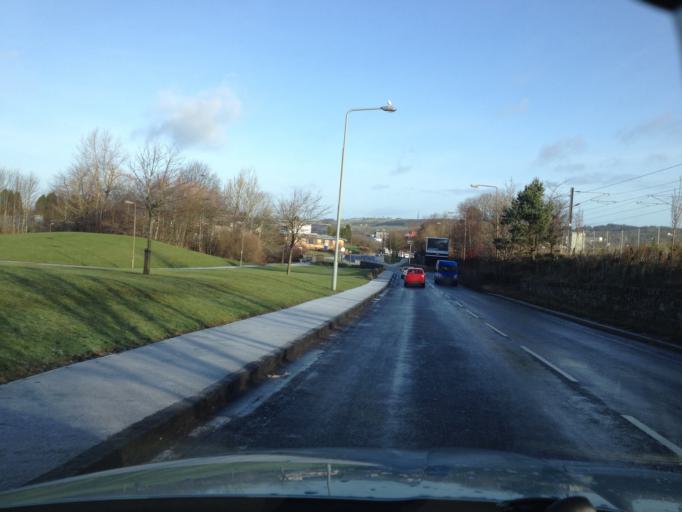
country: GB
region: Scotland
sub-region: West Lothian
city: Bathgate
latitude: 55.8956
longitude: -3.6477
